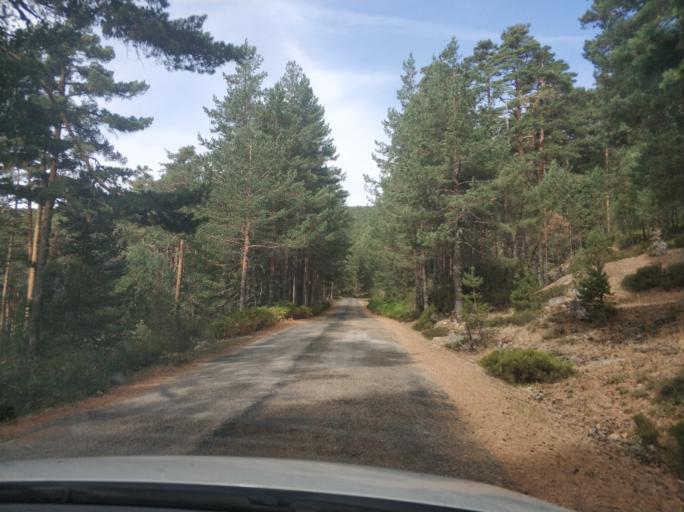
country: ES
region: Castille and Leon
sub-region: Provincia de Soria
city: Duruelo de la Sierra
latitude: 41.9946
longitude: -2.9188
